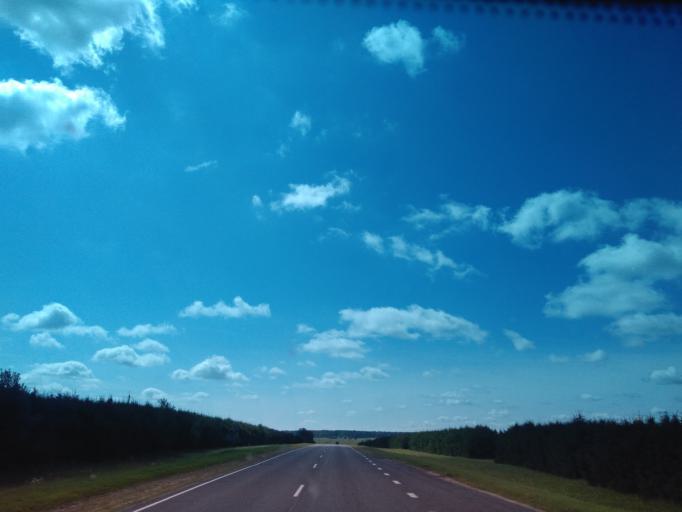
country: BY
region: Minsk
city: Uzda
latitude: 53.3744
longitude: 27.2355
